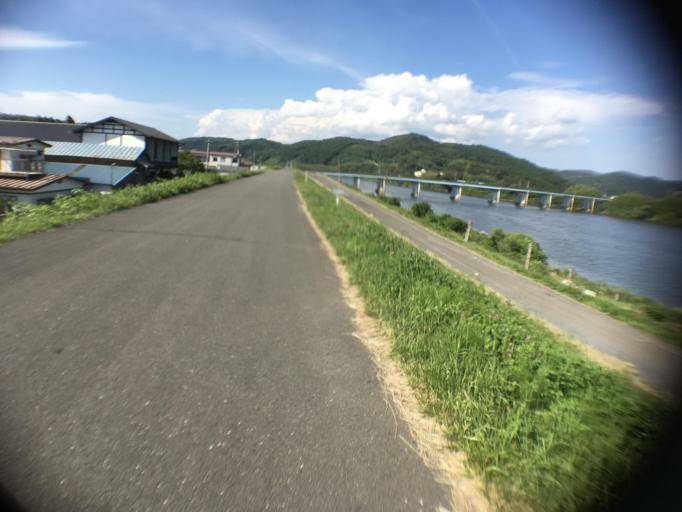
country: JP
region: Miyagi
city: Wakuya
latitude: 38.6513
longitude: 141.2827
